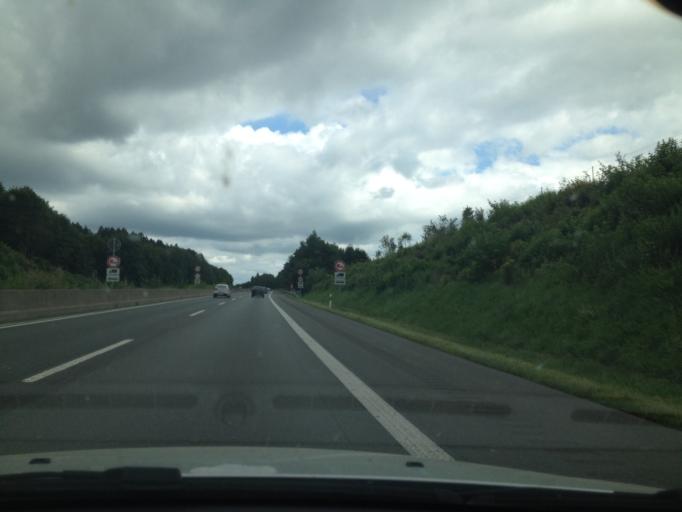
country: DE
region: North Rhine-Westphalia
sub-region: Regierungsbezirk Arnsberg
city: Drolshagen
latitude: 50.9742
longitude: 7.7395
